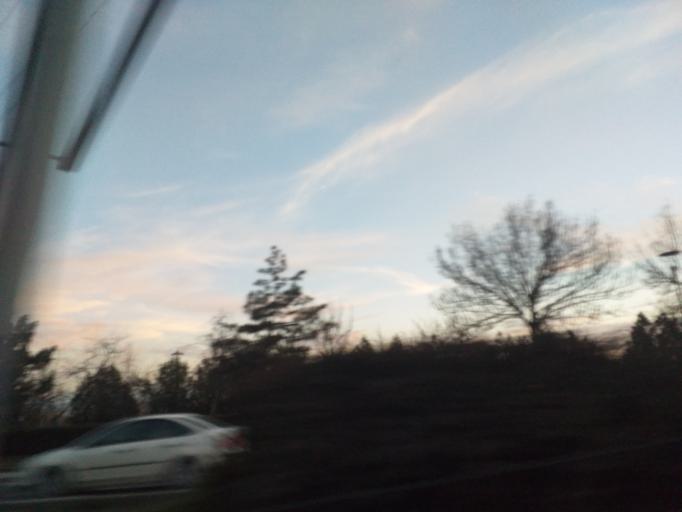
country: TR
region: Ankara
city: Ankara
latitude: 39.9528
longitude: 32.8030
